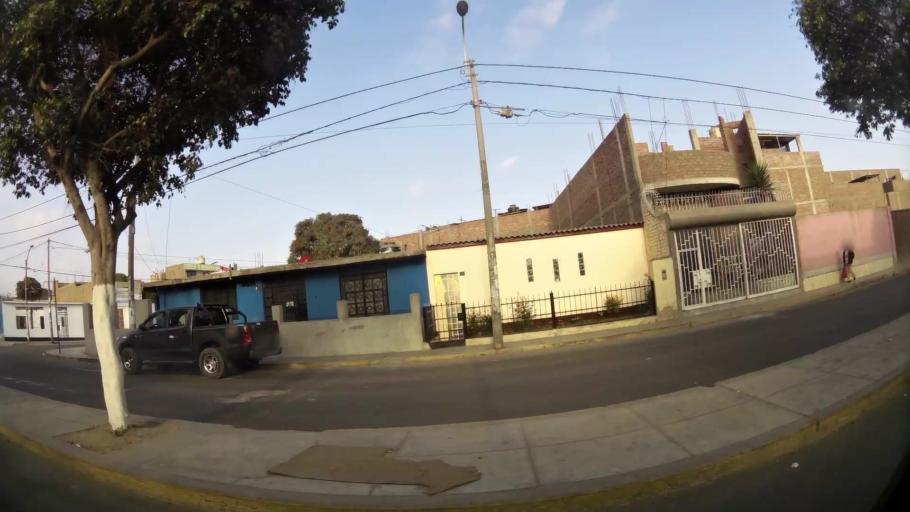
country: PE
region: La Libertad
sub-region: Provincia de Trujillo
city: El Porvenir
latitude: -8.0970
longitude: -79.0162
